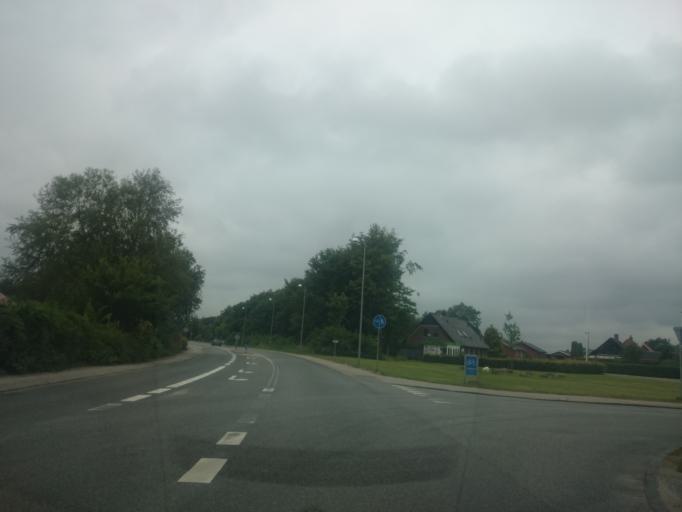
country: DK
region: South Denmark
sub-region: Billund Kommune
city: Grindsted
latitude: 55.6969
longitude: 8.9946
